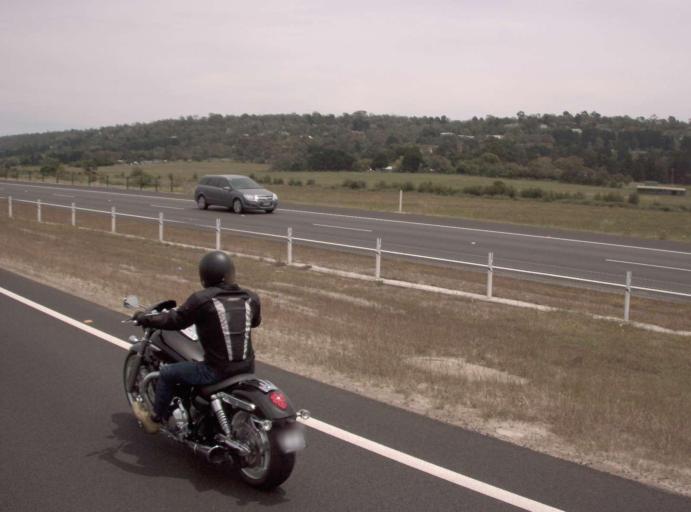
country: AU
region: Victoria
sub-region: Mornington Peninsula
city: Baxter
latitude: -38.2005
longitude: 145.1413
